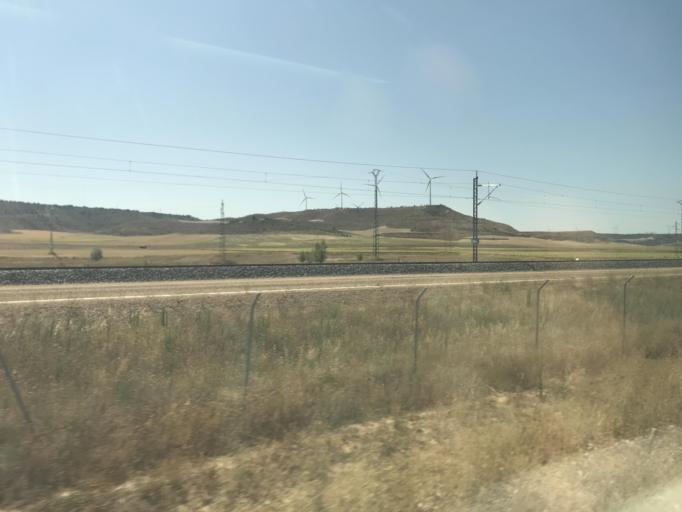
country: ES
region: Castille and Leon
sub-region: Provincia de Palencia
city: Torquemada
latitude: 42.0273
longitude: -4.2808
